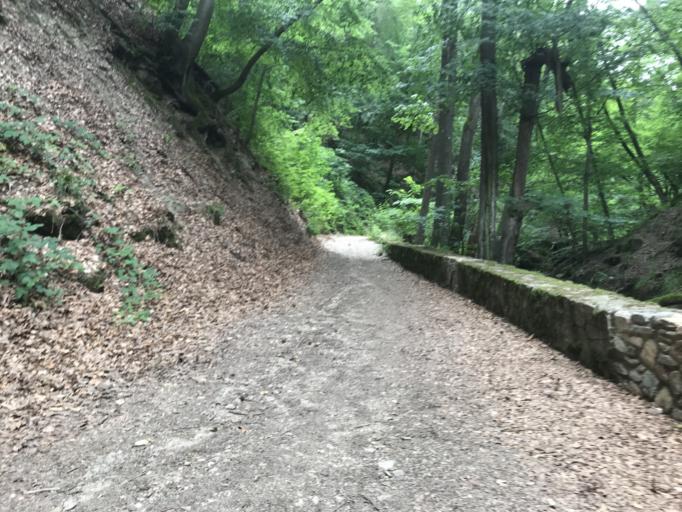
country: DE
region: Rheinland-Pfalz
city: Trechtingshausen
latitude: 49.9990
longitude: 7.8481
